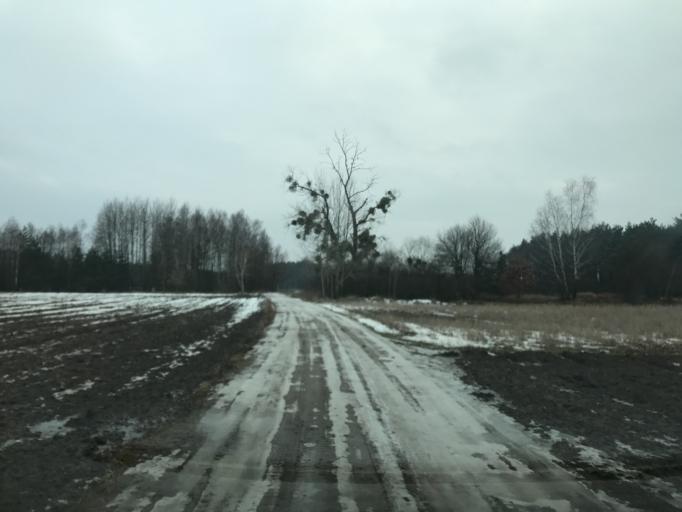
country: PL
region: Kujawsko-Pomorskie
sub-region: Powiat brodnicki
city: Brzozie
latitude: 53.2965
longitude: 19.5653
